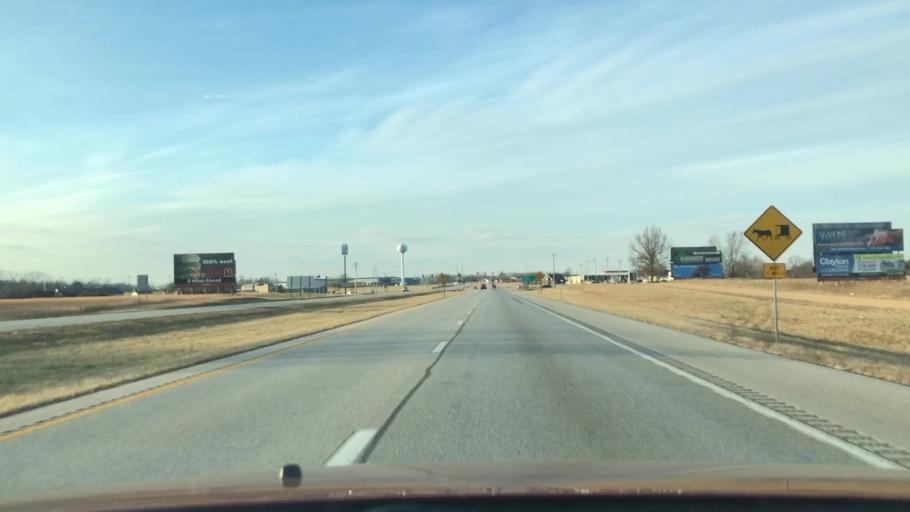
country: US
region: Missouri
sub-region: Webster County
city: Seymour
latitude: 37.1476
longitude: -92.7508
